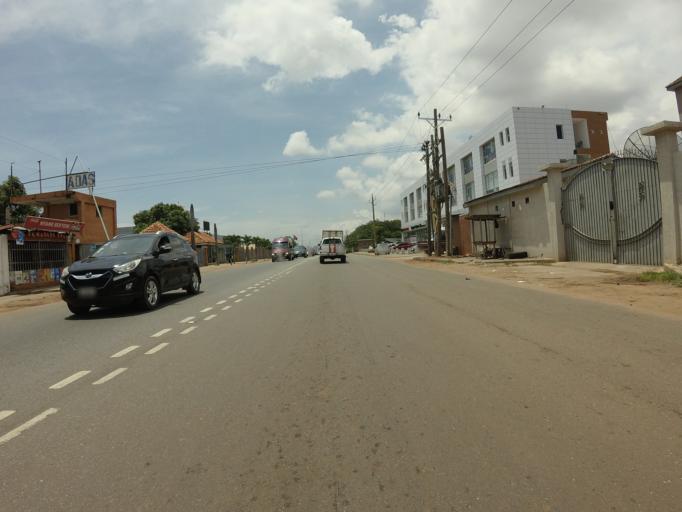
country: GH
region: Greater Accra
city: Medina Estates
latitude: 5.6355
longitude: -0.1321
